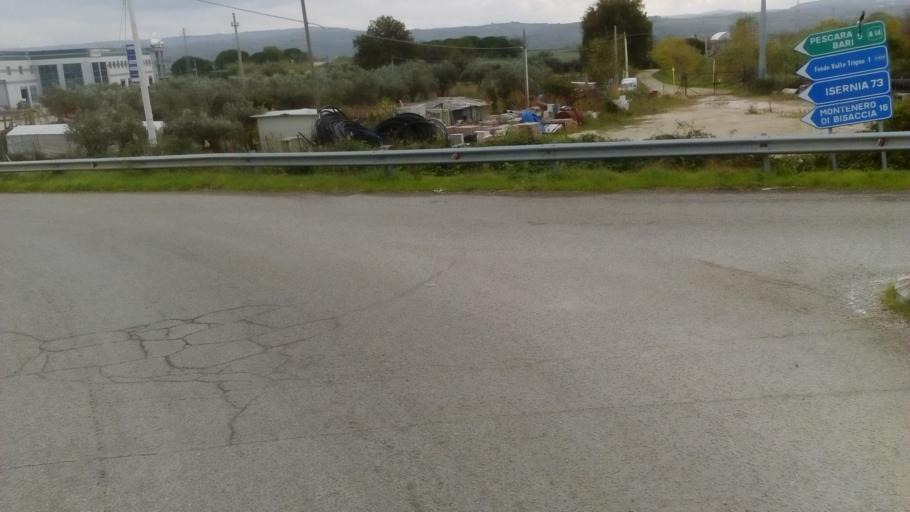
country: IT
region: Abruzzo
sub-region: Provincia di Chieti
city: San Salvo
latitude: 42.0333
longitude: 14.7409
